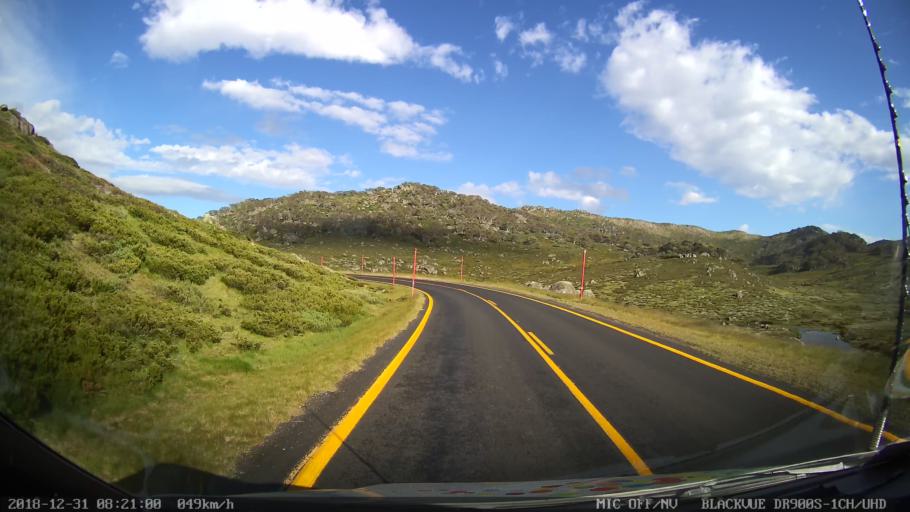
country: AU
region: New South Wales
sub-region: Snowy River
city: Jindabyne
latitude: -36.4260
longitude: 148.3708
